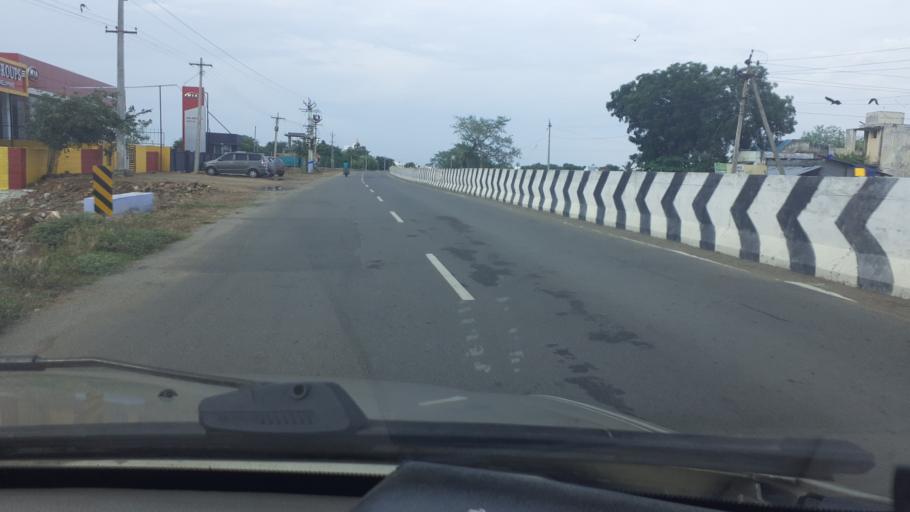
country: IN
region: Tamil Nadu
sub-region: Tirunelveli Kattabo
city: Tirunelveli
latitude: 8.6614
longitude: 77.7150
